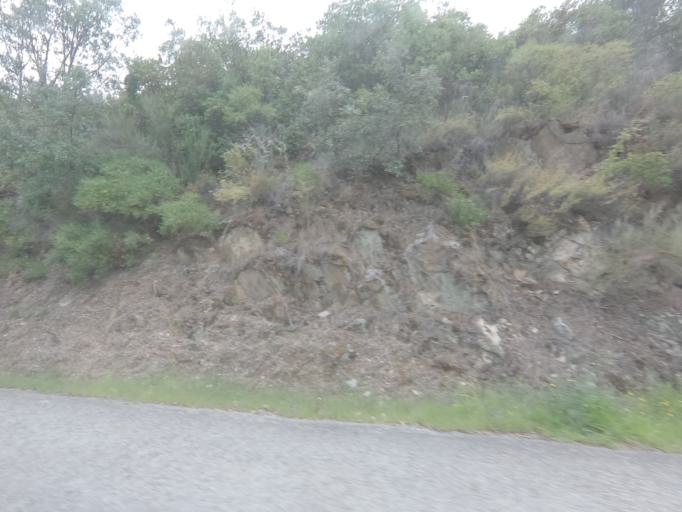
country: PT
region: Viseu
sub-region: Armamar
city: Armamar
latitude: 41.1228
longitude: -7.6547
